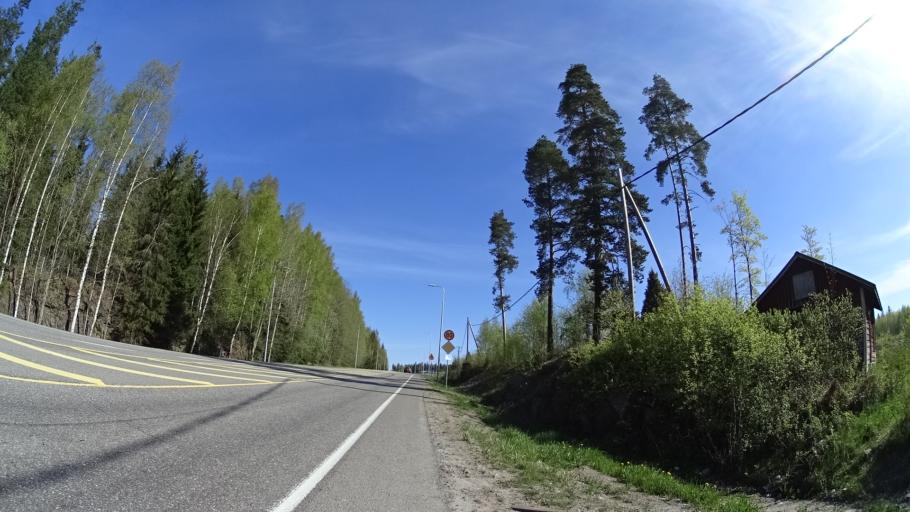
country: FI
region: Uusimaa
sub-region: Helsinki
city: Nurmijaervi
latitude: 60.4384
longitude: 24.8314
